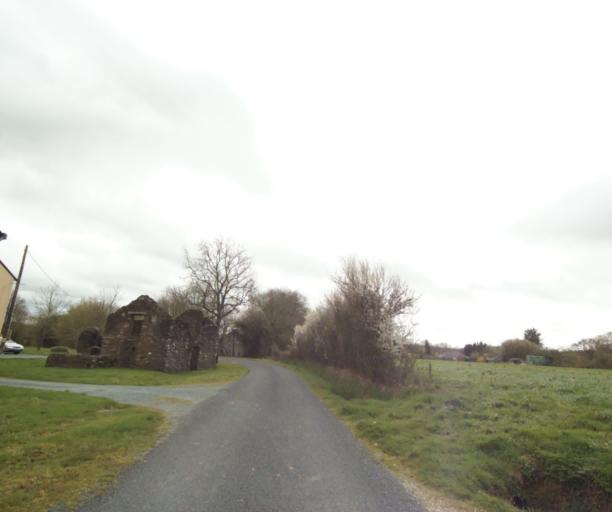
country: FR
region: Pays de la Loire
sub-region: Departement de la Loire-Atlantique
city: Bouvron
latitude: 47.4258
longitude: -1.8656
